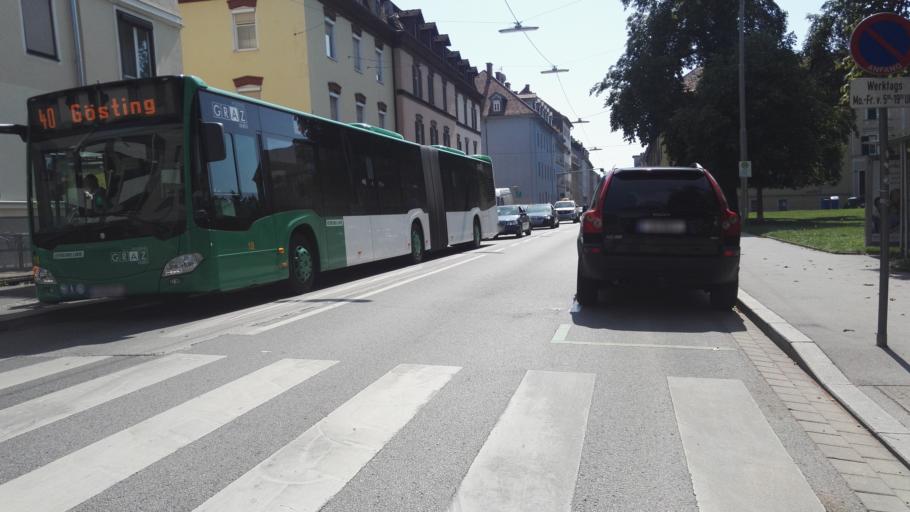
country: AT
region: Styria
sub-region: Graz Stadt
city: Goesting
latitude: 47.0841
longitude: 15.4187
